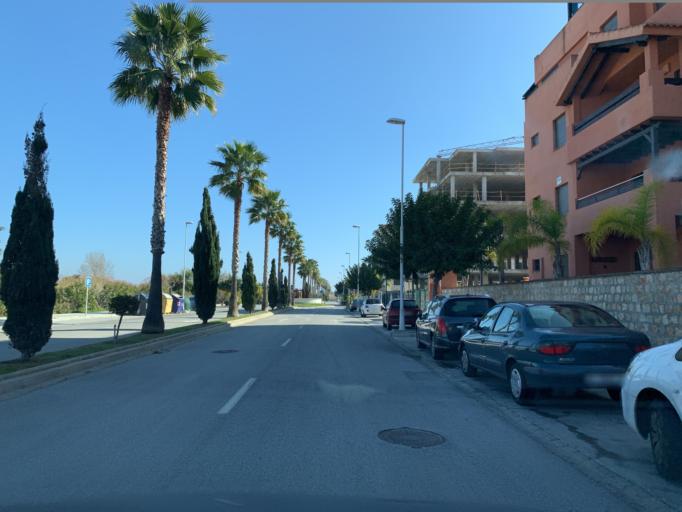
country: ES
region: Andalusia
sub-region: Provincia de Granada
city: El Varadero
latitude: 36.7216
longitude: -3.5536
